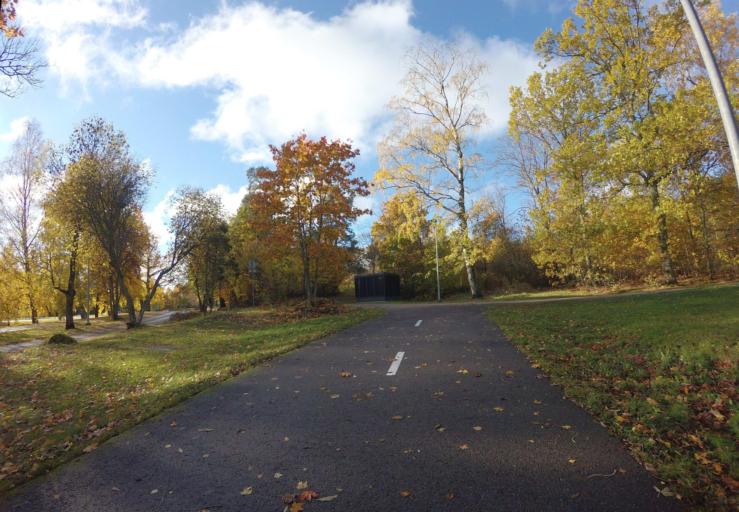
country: FI
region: Varsinais-Suomi
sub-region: Turku
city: Naantali
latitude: 60.4243
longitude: 22.0951
